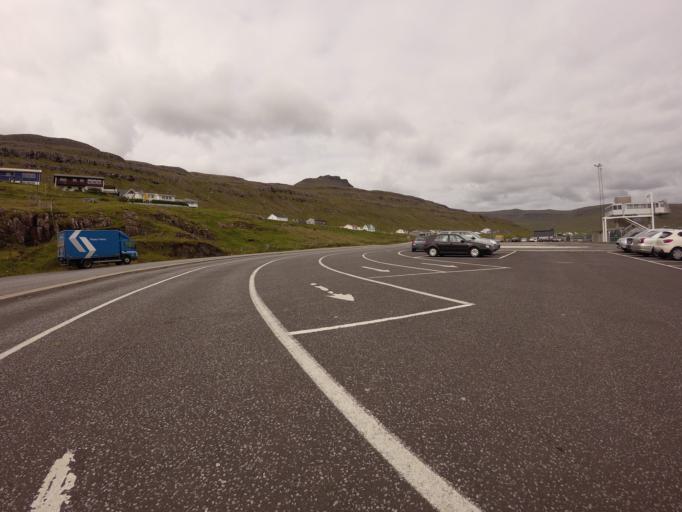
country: FO
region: Suduroy
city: Tvoroyri
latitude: 61.5478
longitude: -6.8173
